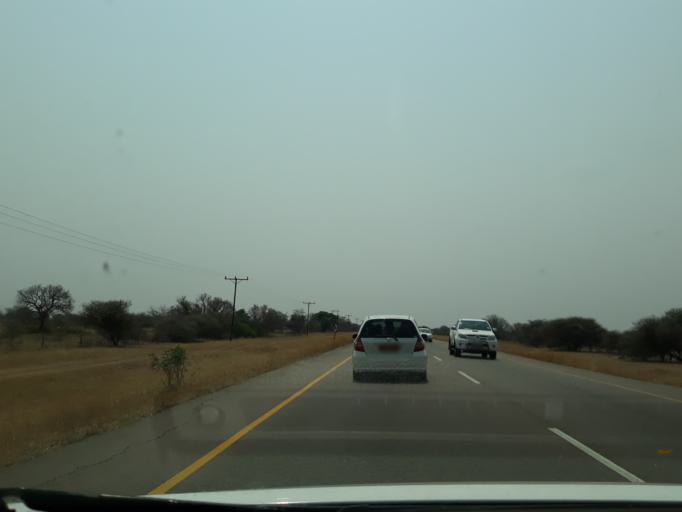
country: BW
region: Kgatleng
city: Mochudi
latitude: -24.2978
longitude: 26.1288
